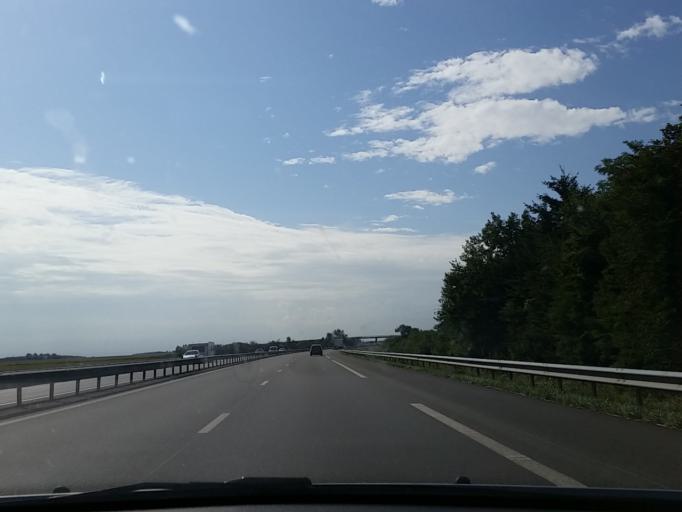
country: FR
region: Centre
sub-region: Departement du Cher
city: Levet
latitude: 46.9355
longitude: 2.4220
